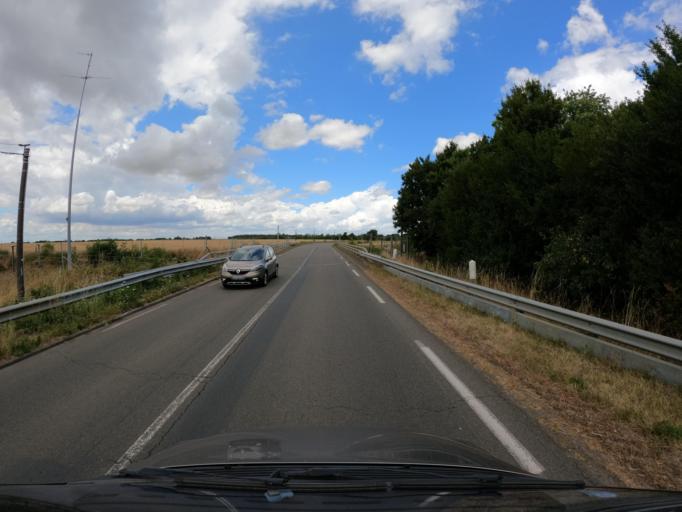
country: FR
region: Pays de la Loire
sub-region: Departement de la Sarthe
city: Sable-sur-Sarthe
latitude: 47.8551
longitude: -0.3232
